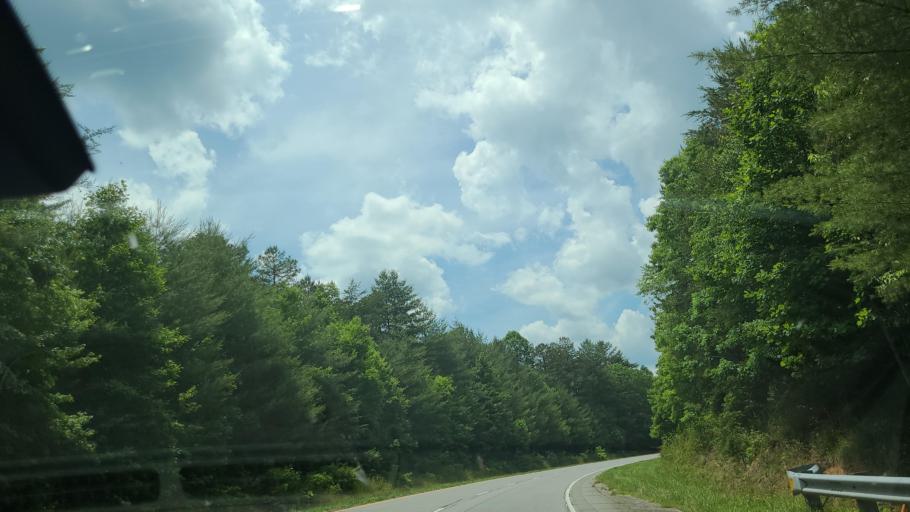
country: US
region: Georgia
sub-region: Fannin County
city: McCaysville
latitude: 35.0115
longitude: -84.2647
